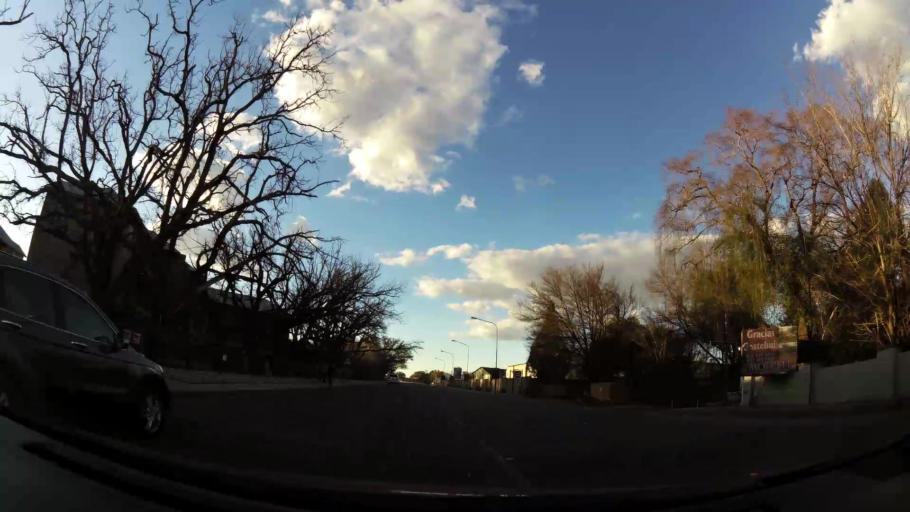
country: ZA
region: North-West
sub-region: Dr Kenneth Kaunda District Municipality
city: Potchefstroom
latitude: -26.6828
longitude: 27.1020
